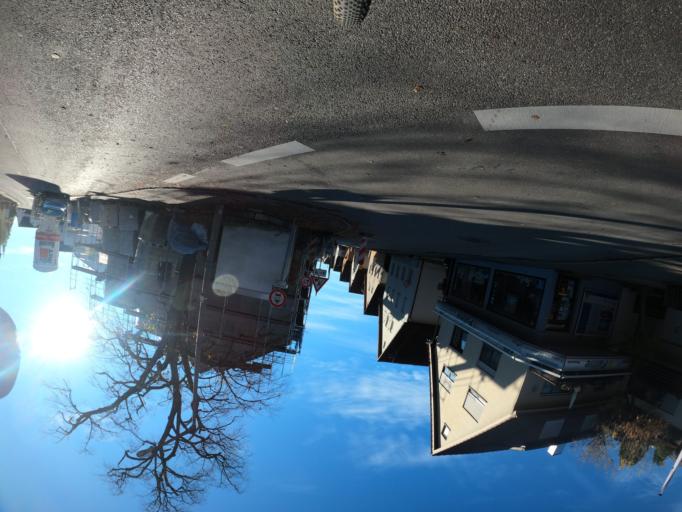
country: DE
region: Baden-Wuerttemberg
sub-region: Regierungsbezirk Stuttgart
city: Magstadt
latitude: 48.7391
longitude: 8.9631
